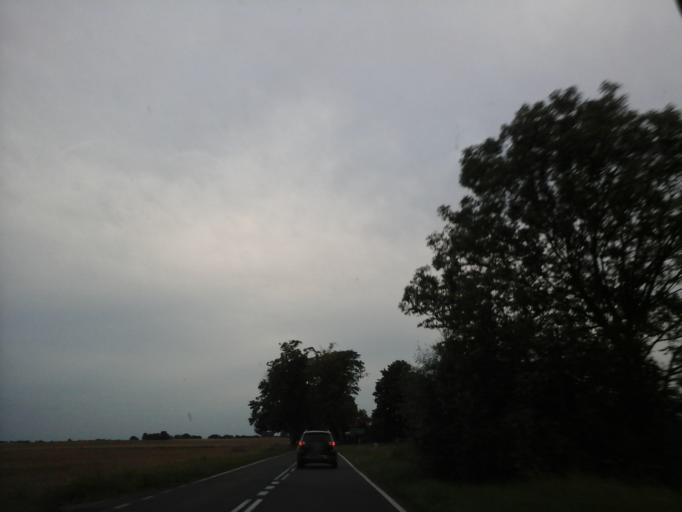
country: PL
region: West Pomeranian Voivodeship
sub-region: Powiat stargardzki
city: Stargard Szczecinski
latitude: 53.3756
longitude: 15.0792
